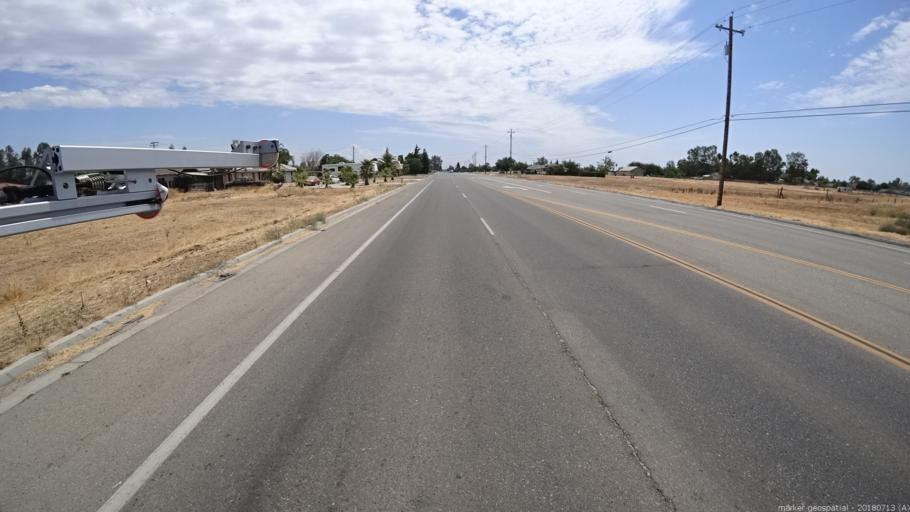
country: US
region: California
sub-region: Madera County
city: Madera Acres
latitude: 36.9965
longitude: -120.0879
